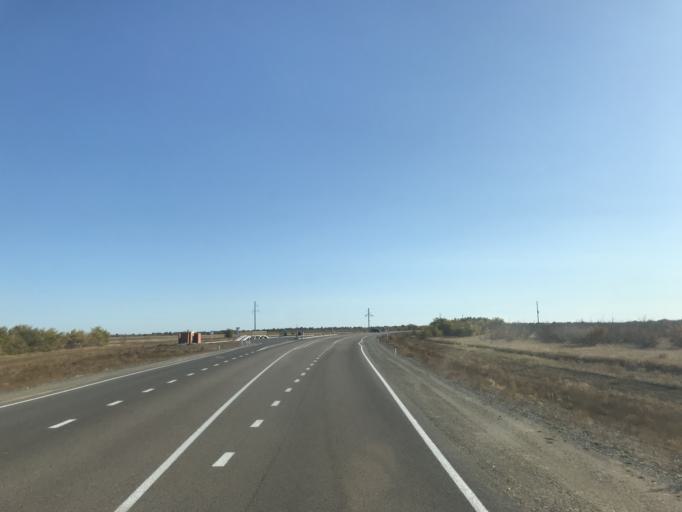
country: KZ
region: Pavlodar
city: Koktobe
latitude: 51.7295
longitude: 77.5583
